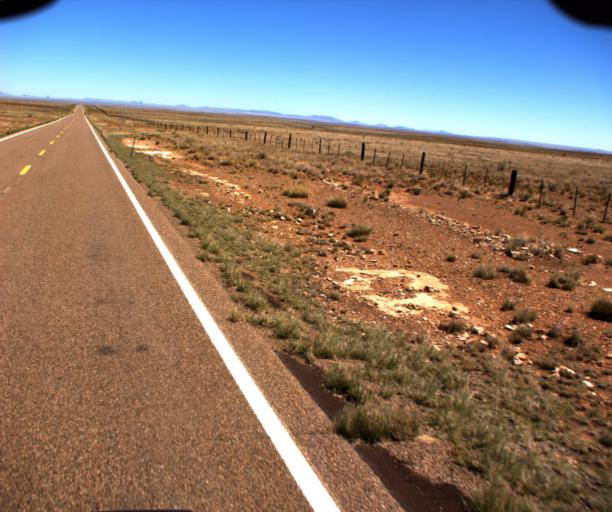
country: US
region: Arizona
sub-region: Navajo County
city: Winslow
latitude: 34.8725
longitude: -110.6558
